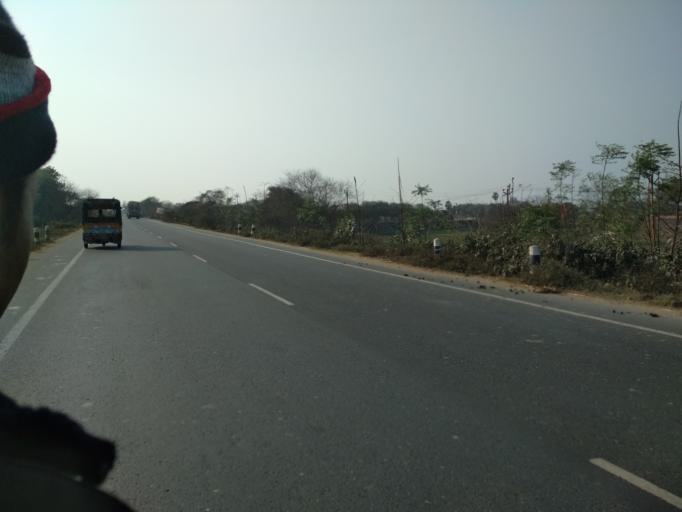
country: IN
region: Bihar
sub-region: Khagaria
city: Khagaria
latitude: 25.5073
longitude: 86.5521
